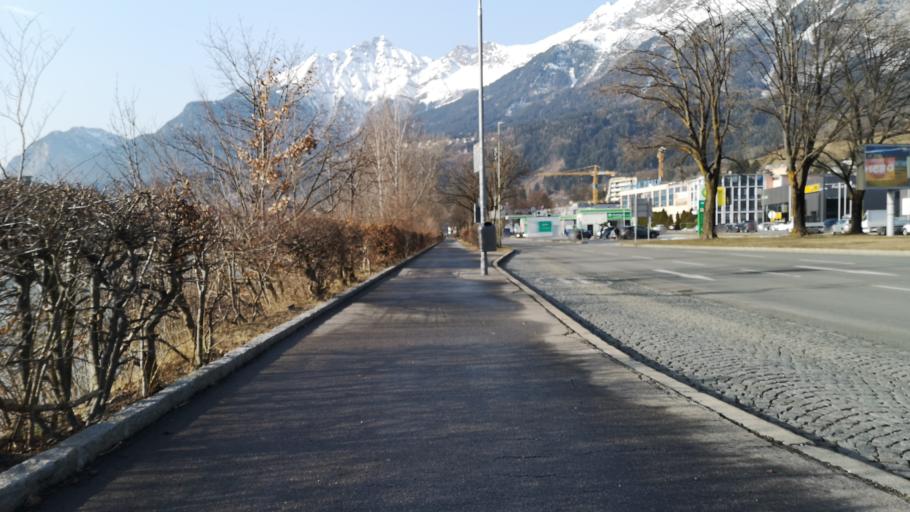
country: AT
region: Tyrol
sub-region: Politischer Bezirk Innsbruck Land
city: Rum
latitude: 47.2763
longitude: 11.4260
